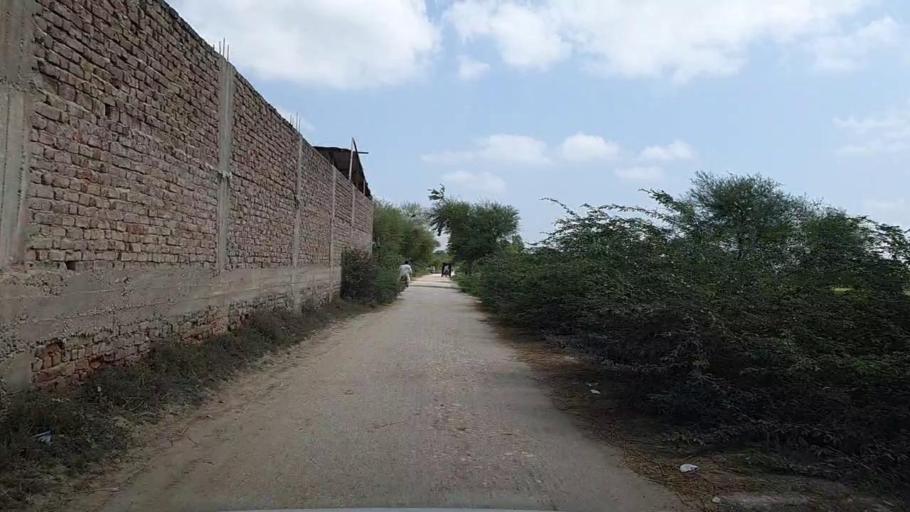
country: PK
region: Sindh
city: Kario
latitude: 24.6754
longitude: 68.5376
